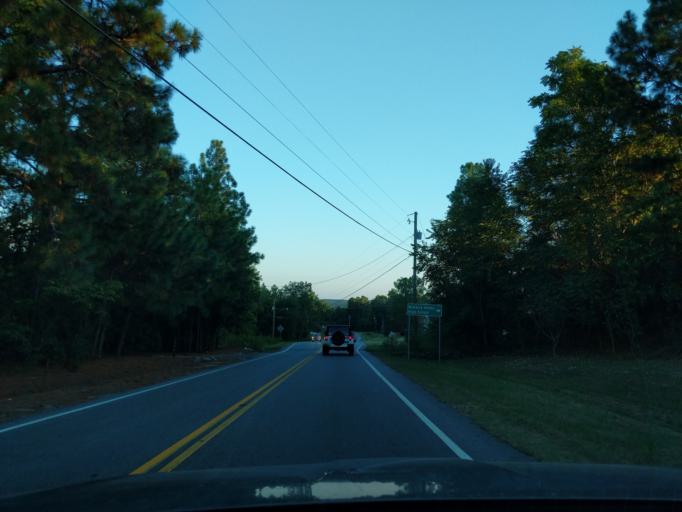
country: US
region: South Carolina
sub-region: Aiken County
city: Burnettown
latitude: 33.5340
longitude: -81.8613
